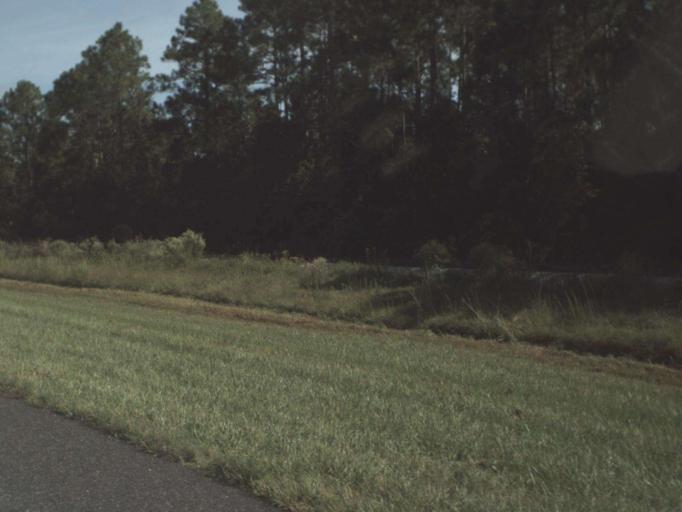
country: US
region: Florida
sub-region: Bay County
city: Youngstown
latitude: 30.4236
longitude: -85.4290
